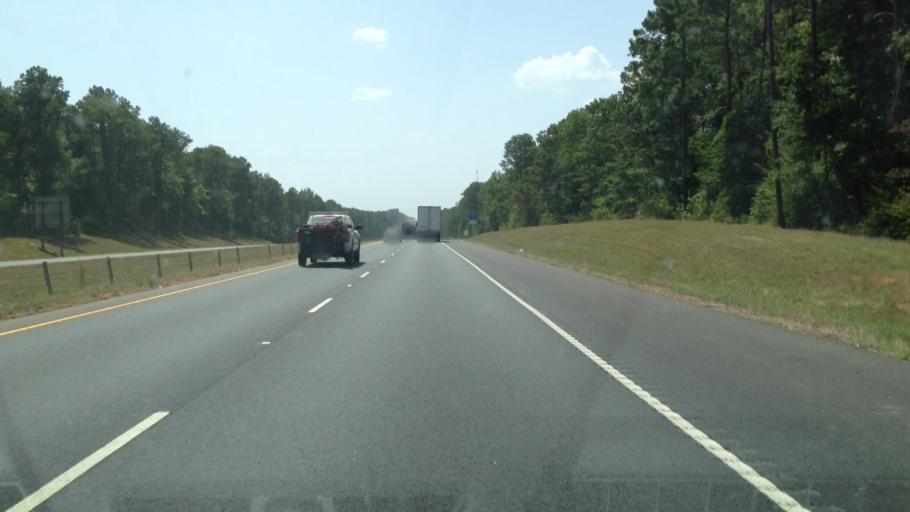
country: US
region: Louisiana
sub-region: Webster Parish
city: Minden
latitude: 32.5728
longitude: -93.2107
